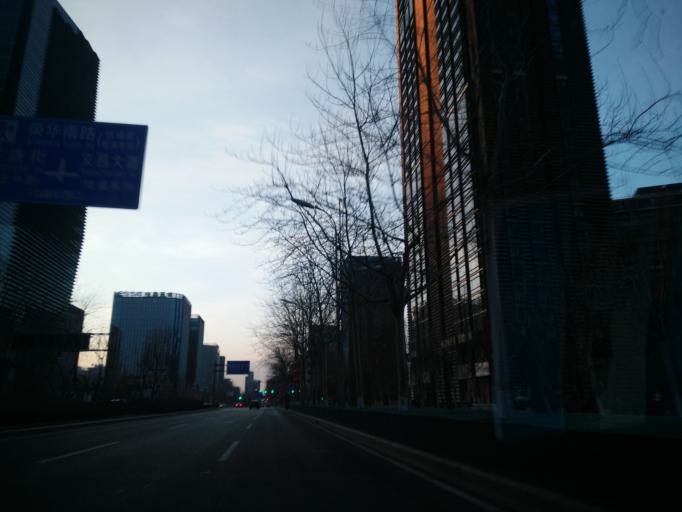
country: CN
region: Beijing
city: Jiugong
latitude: 39.7901
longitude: 116.5050
